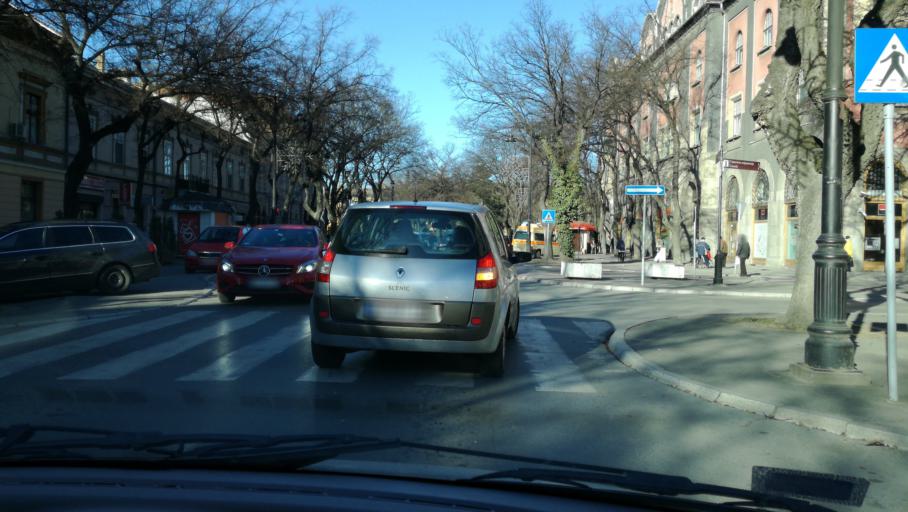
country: RS
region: Autonomna Pokrajina Vojvodina
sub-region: Severnobacki Okrug
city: Subotica
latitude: 46.0989
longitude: 19.6643
